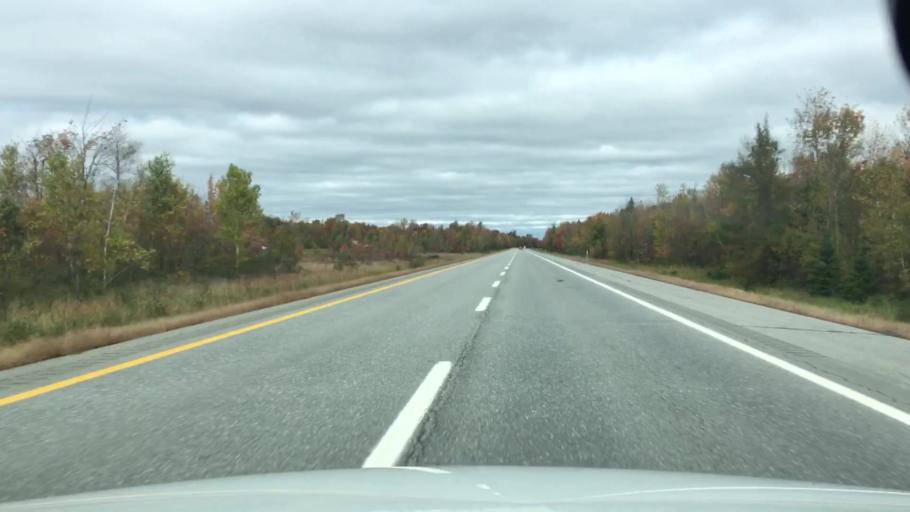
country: US
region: Maine
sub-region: Waldo County
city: Burnham
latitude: 44.6860
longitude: -69.4740
